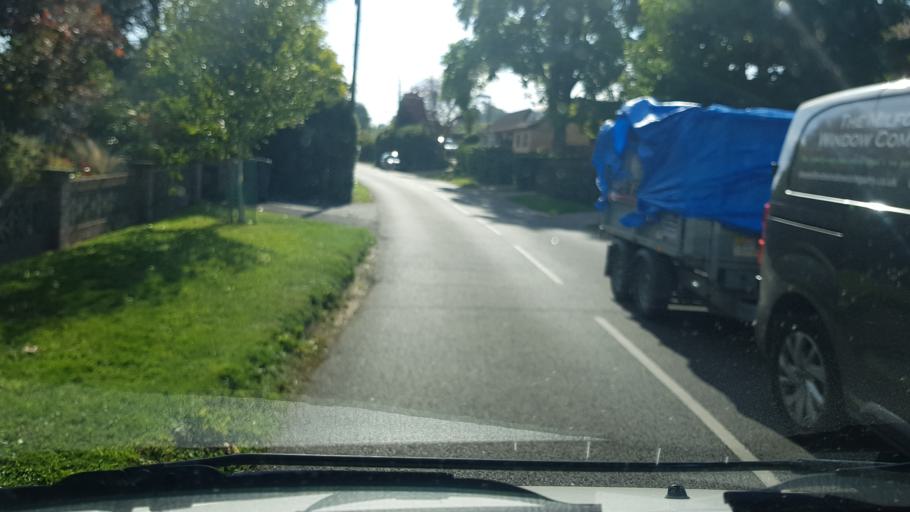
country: GB
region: England
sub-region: Surrey
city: Godalming
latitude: 51.2040
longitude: -0.6167
